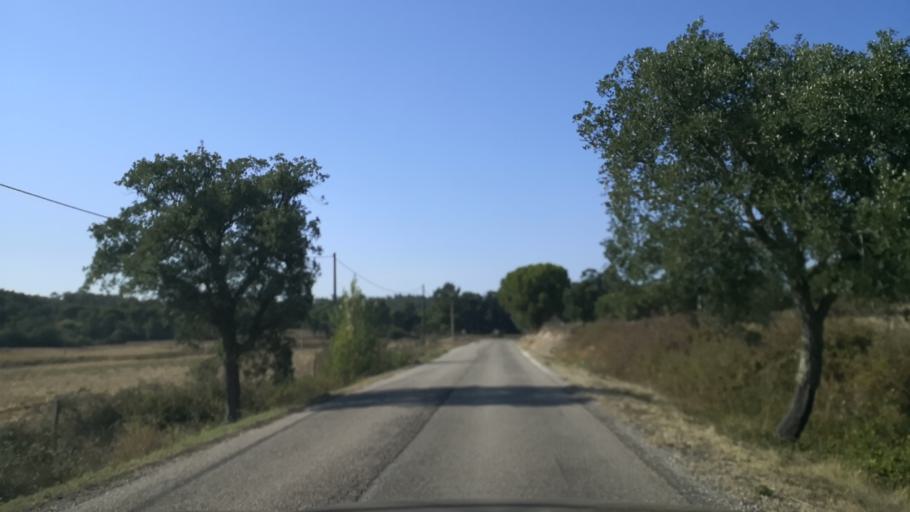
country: PT
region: Santarem
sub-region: Coruche
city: Coruche
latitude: 38.8765
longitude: -8.5399
